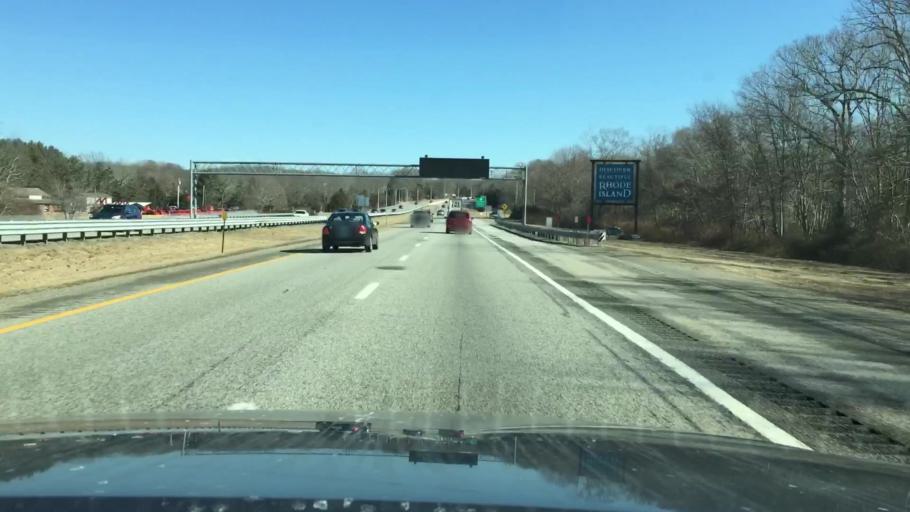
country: US
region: Rhode Island
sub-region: Washington County
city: Ashaway
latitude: 41.4433
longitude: -71.7951
